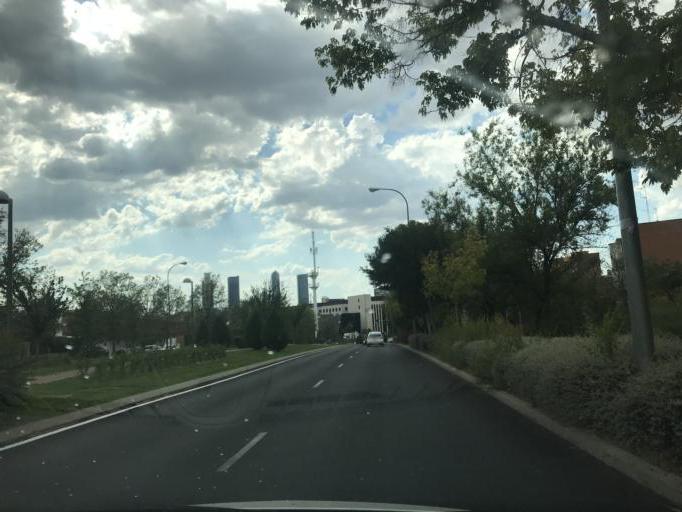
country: ES
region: Madrid
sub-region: Provincia de Madrid
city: Pinar de Chamartin
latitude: 40.4720
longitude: -3.6607
